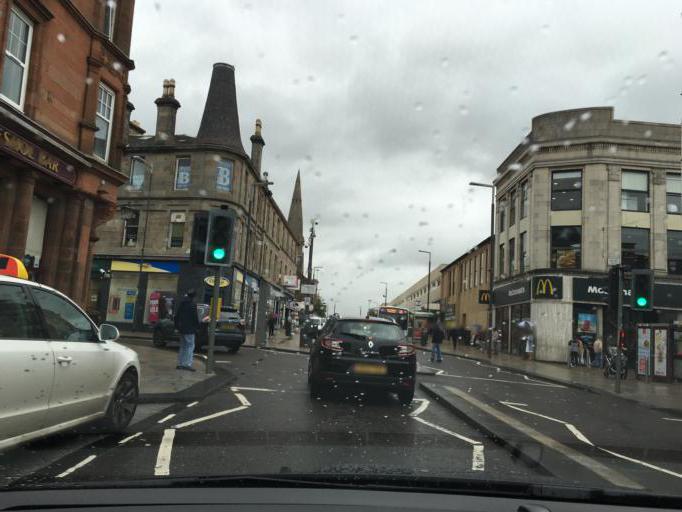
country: GB
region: Scotland
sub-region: North Lanarkshire
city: Motherwell
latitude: 55.7903
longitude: -3.9932
